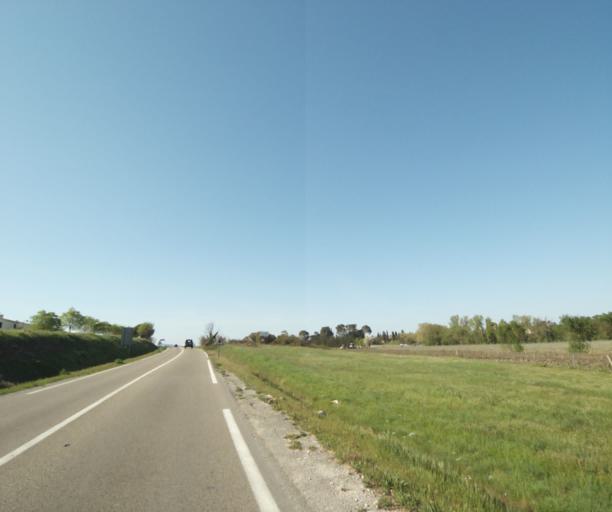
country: FR
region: Languedoc-Roussillon
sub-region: Departement de l'Herault
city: Jacou
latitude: 43.6629
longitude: 3.9255
